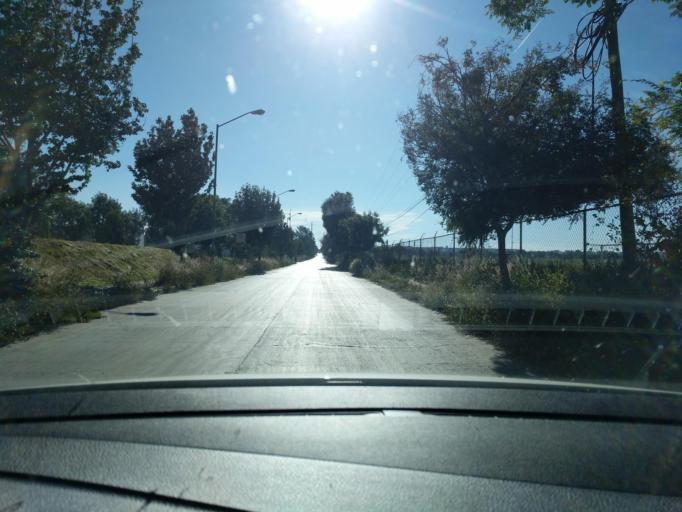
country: MX
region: Puebla
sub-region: Huejotzingo
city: Los Encinos
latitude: 19.1753
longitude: -98.3874
